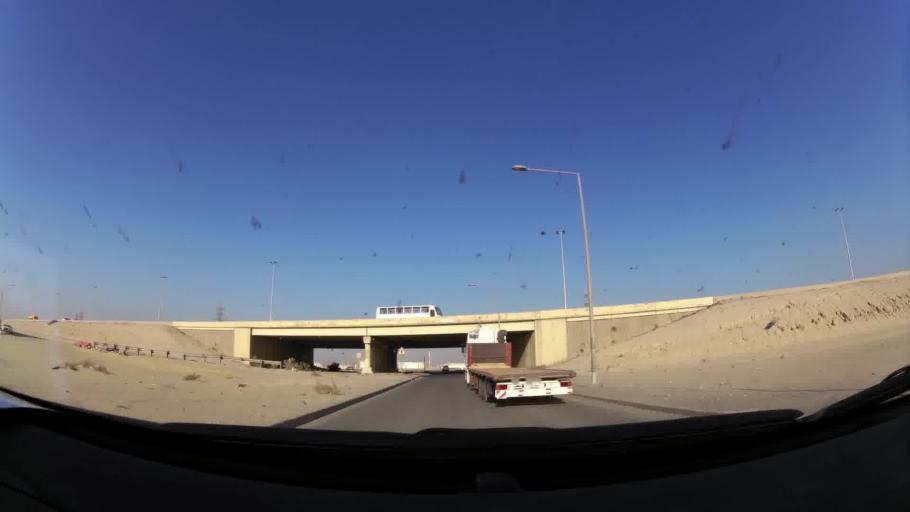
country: KW
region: Al Ahmadi
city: Al Fahahil
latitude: 29.0103
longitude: 48.1322
